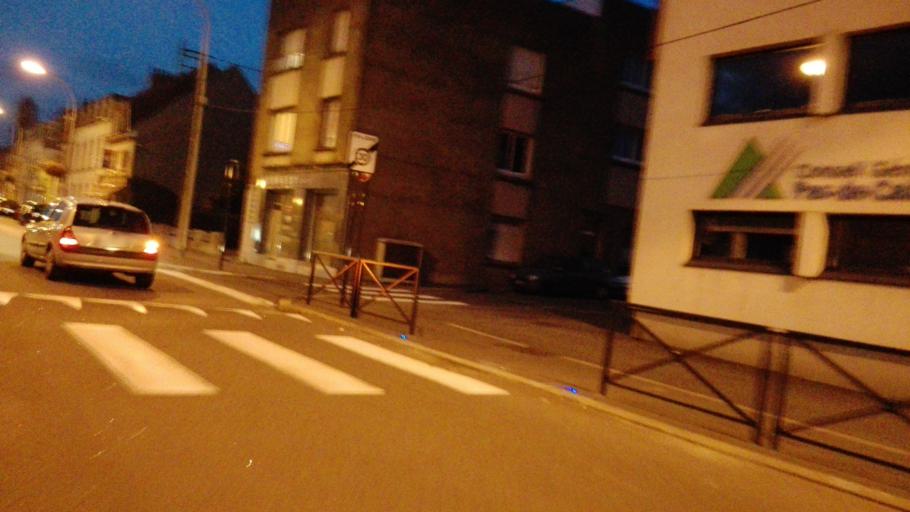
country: FR
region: Nord-Pas-de-Calais
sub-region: Departement du Pas-de-Calais
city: Boulogne-sur-Mer
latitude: 50.7154
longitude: 1.6141
